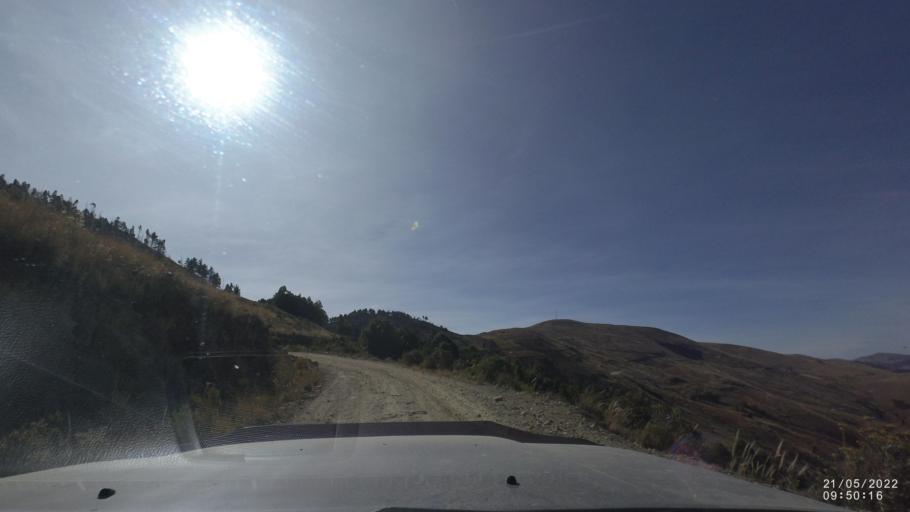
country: BO
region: Cochabamba
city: Colomi
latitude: -17.3439
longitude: -65.9937
